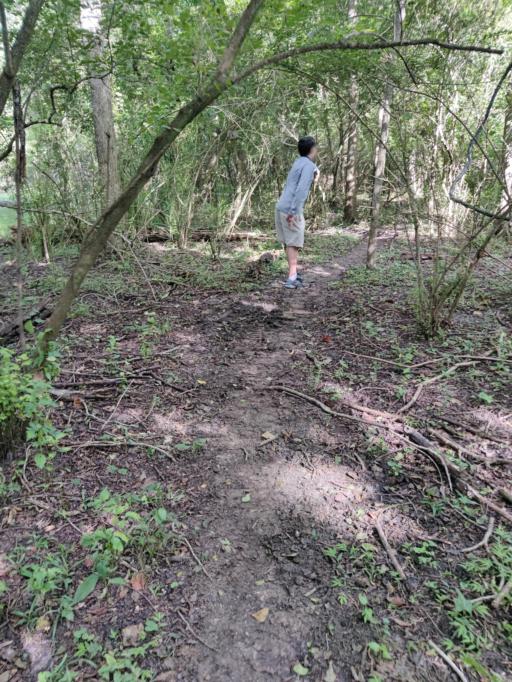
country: US
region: Texas
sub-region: Harris County
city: Oak Cliff Place
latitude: 29.8327
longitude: -95.6649
